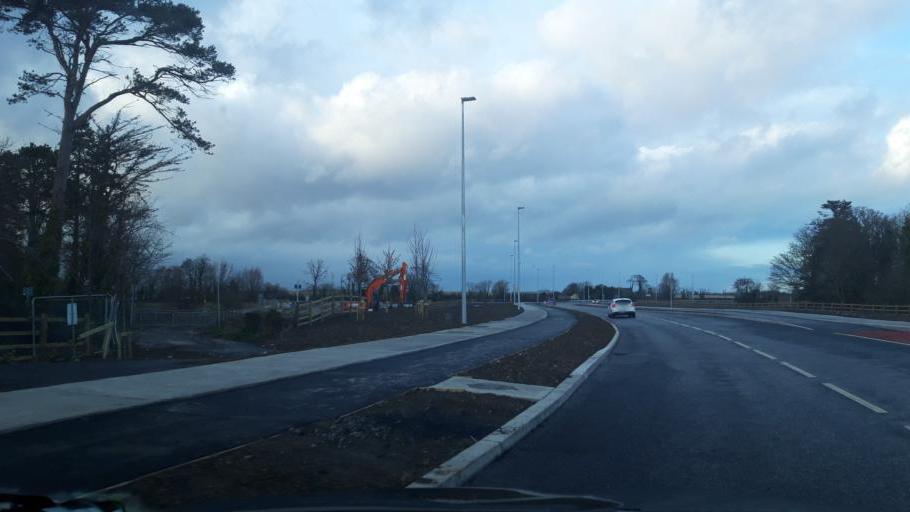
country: IE
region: Leinster
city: Portraine
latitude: 53.4899
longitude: -6.1308
